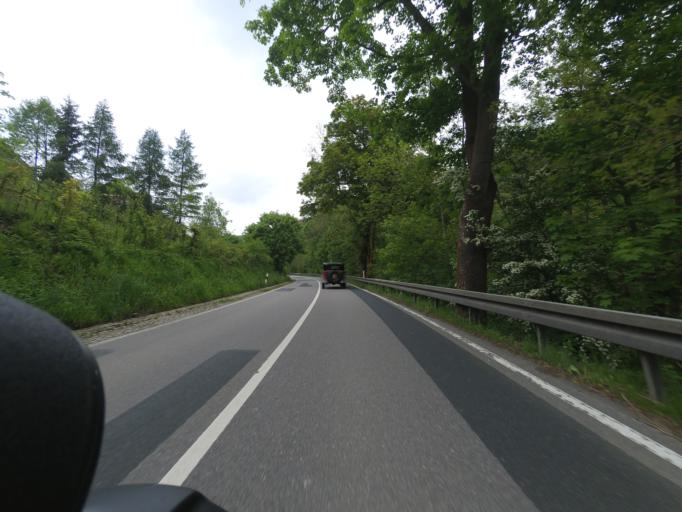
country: DE
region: Saxony
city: Scharfenstein
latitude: 50.6931
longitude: 13.0613
